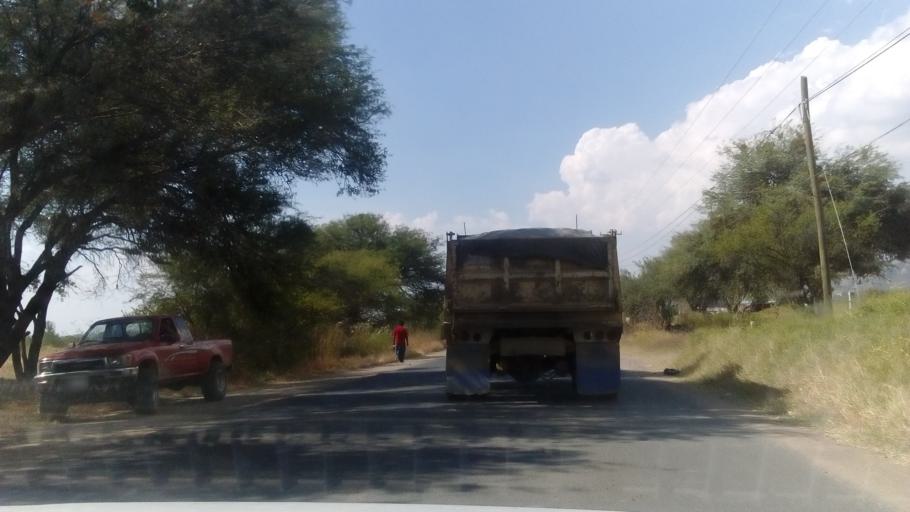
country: MX
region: Guanajuato
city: Duarte
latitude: 21.0906
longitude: -101.5356
